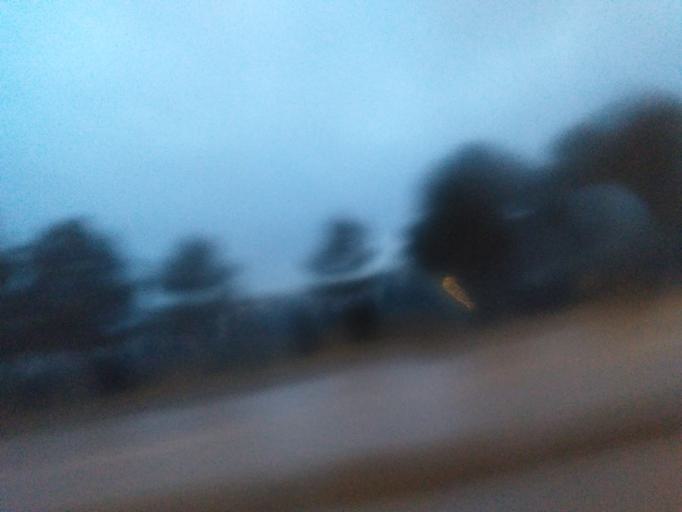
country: TR
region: Ankara
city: Ankara
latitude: 39.9608
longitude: 32.8224
